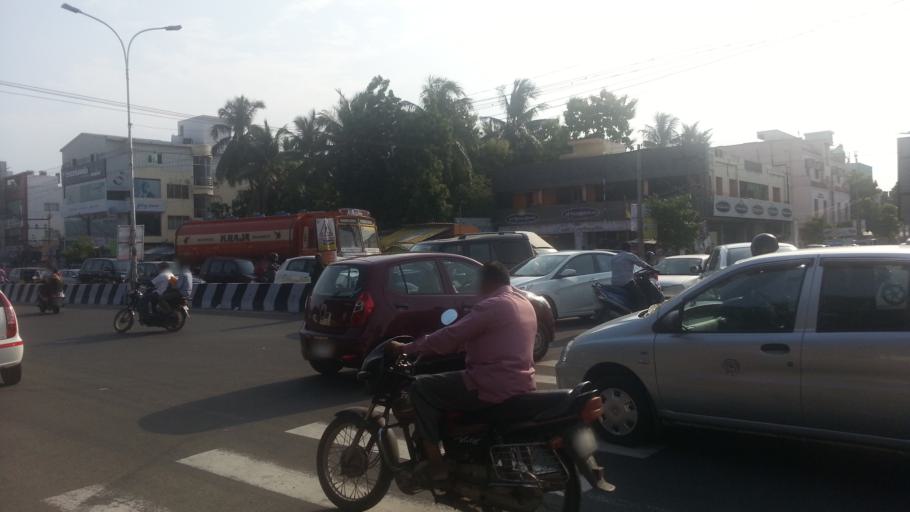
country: IN
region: Tamil Nadu
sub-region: Kancheepuram
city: Alandur
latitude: 12.9896
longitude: 80.2190
